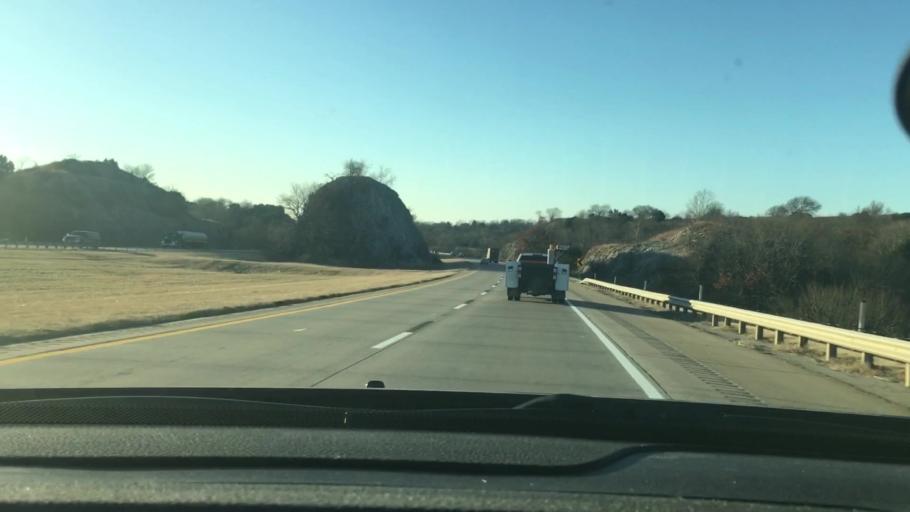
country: US
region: Oklahoma
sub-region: Murray County
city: Davis
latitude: 34.3595
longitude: -97.1488
